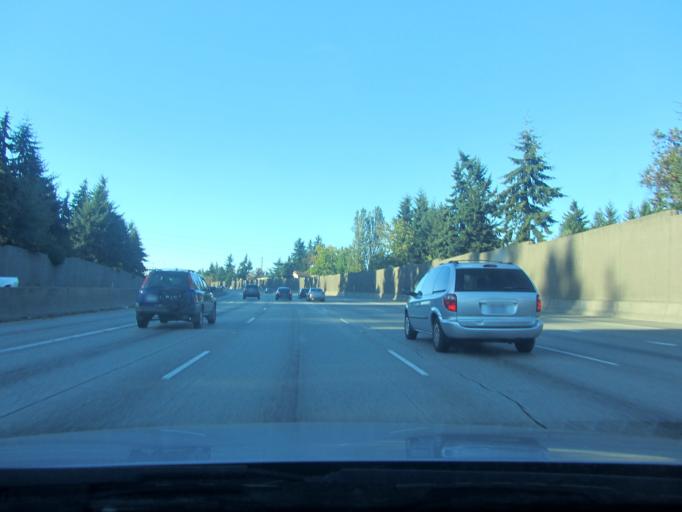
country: US
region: Washington
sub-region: King County
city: Shoreline
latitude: 47.7162
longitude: -122.3252
